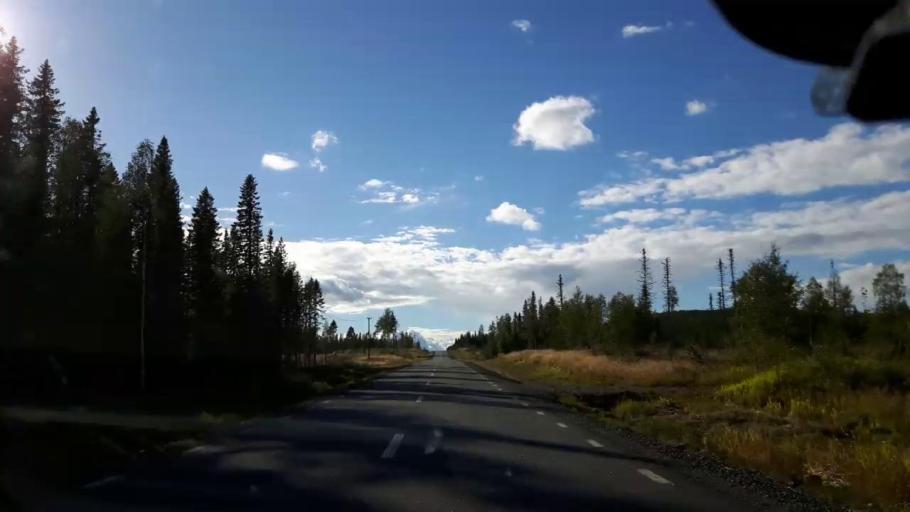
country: SE
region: Jaemtland
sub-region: Stroemsunds Kommun
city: Stroemsund
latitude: 63.5418
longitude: 15.9484
